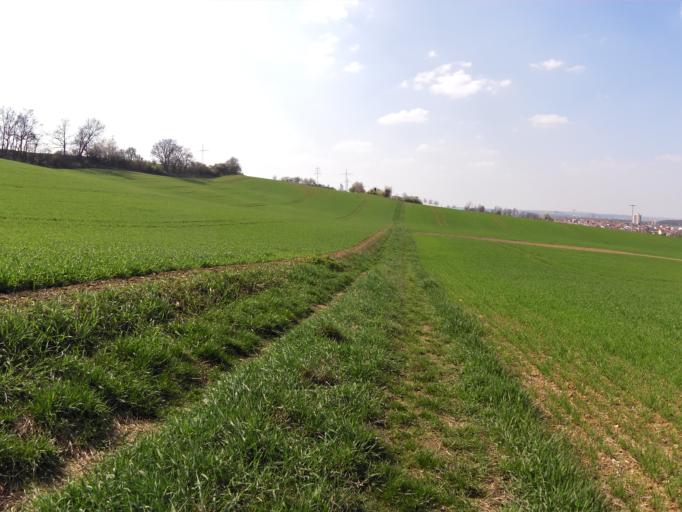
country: DE
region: Bavaria
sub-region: Regierungsbezirk Unterfranken
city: Rottendorf
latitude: 49.7797
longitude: 10.0372
